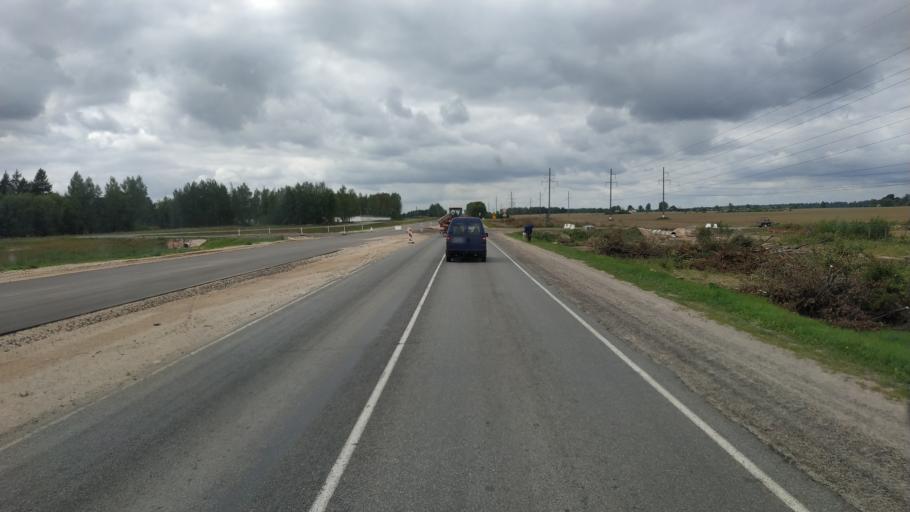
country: BY
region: Mogilev
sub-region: Mahilyowski Rayon
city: Kadino
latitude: 53.8679
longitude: 30.4727
